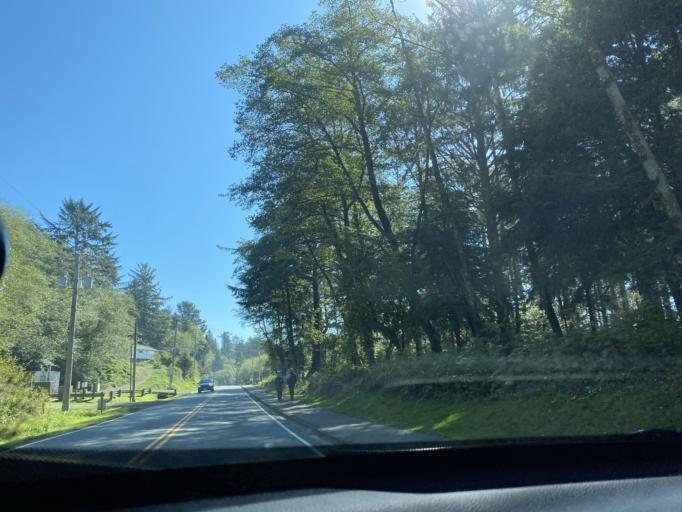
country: US
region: Washington
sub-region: Clallam County
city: Forks
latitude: 47.9053
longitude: -124.6307
